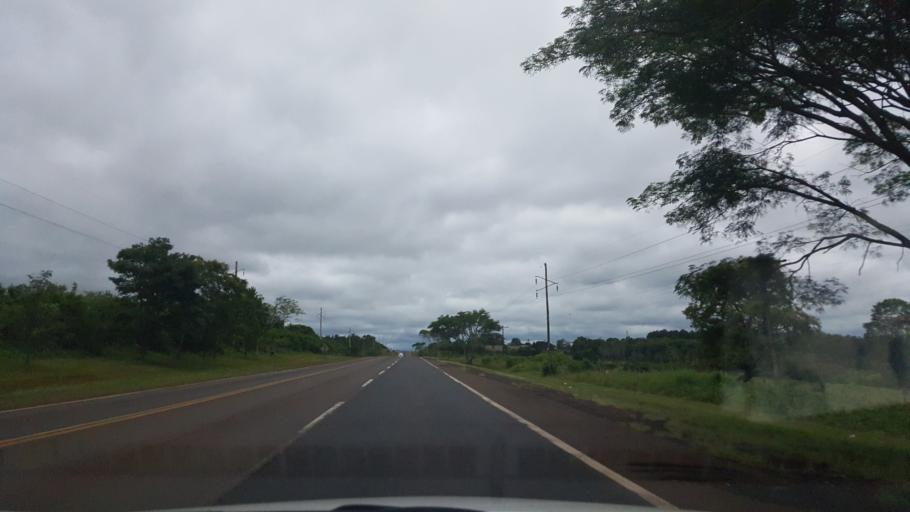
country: AR
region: Misiones
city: Capiovi
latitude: -26.9478
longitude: -55.0886
